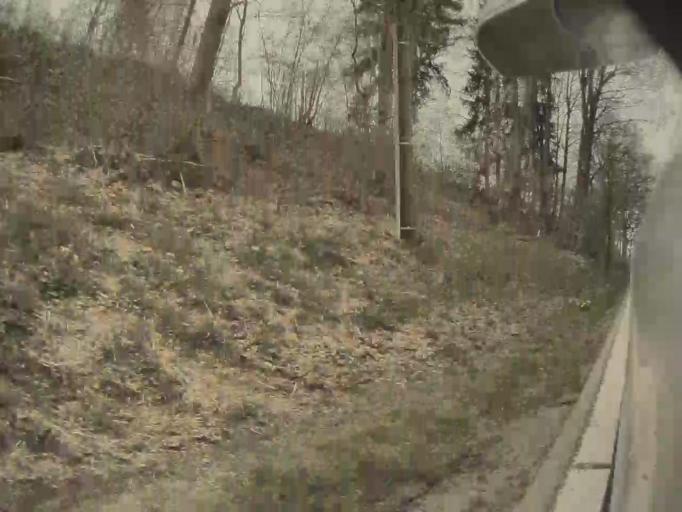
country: BE
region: Wallonia
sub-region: Province de Liege
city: Lierneux
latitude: 50.3235
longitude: 5.7431
